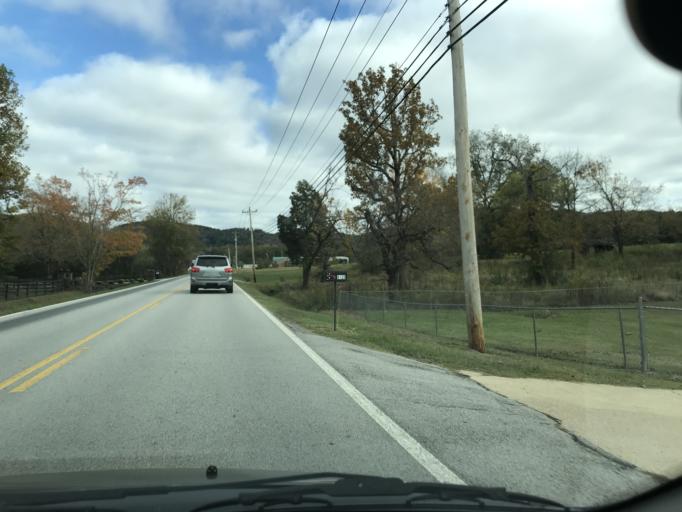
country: US
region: Tennessee
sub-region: Hamilton County
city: Lakesite
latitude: 35.1765
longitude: -85.0321
